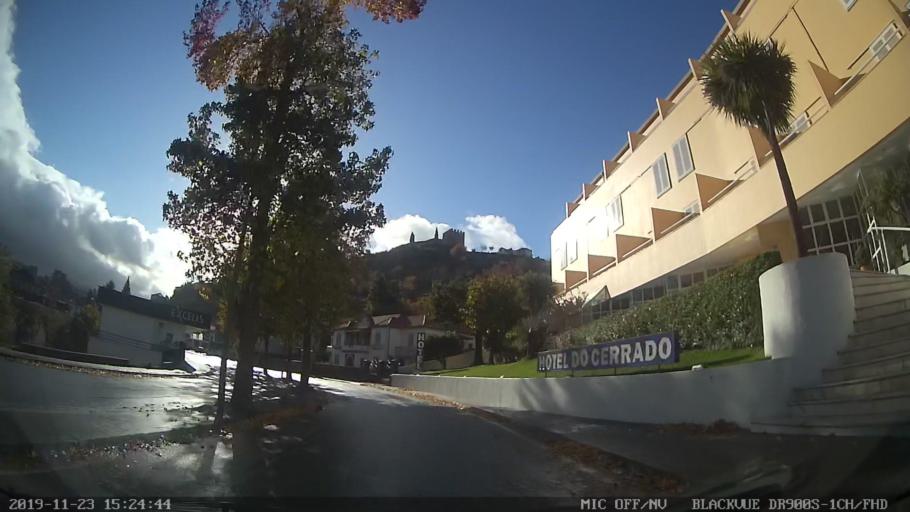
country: PT
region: Viseu
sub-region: Lamego
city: Lamego
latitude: 41.1003
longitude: -7.8064
